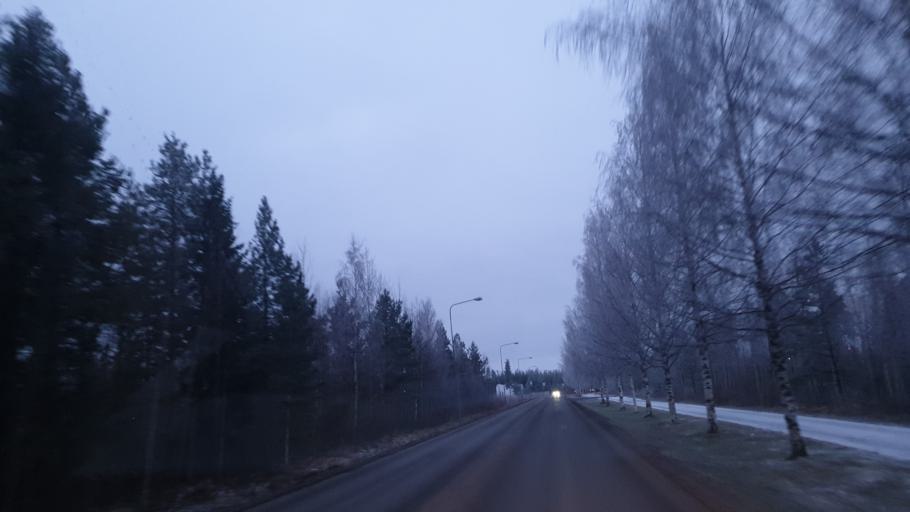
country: FI
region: Southern Ostrobothnia
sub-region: Seinaejoki
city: Nurmo
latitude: 62.7814
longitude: 22.8982
